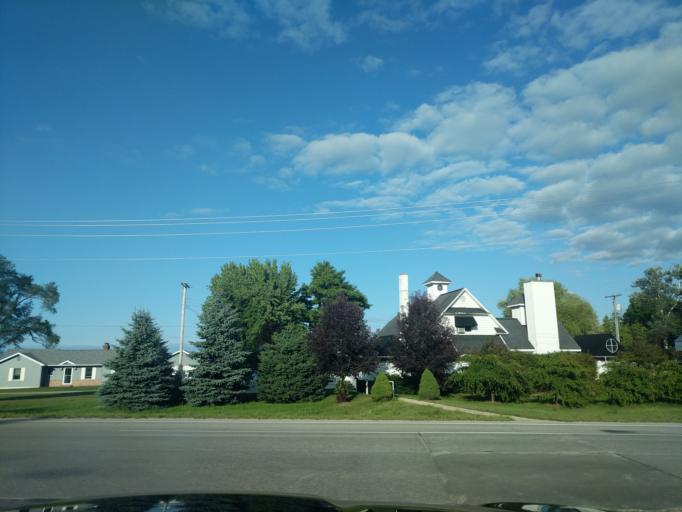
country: US
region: Michigan
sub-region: Leelanau County
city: Leland
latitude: 44.9709
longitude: -85.6493
